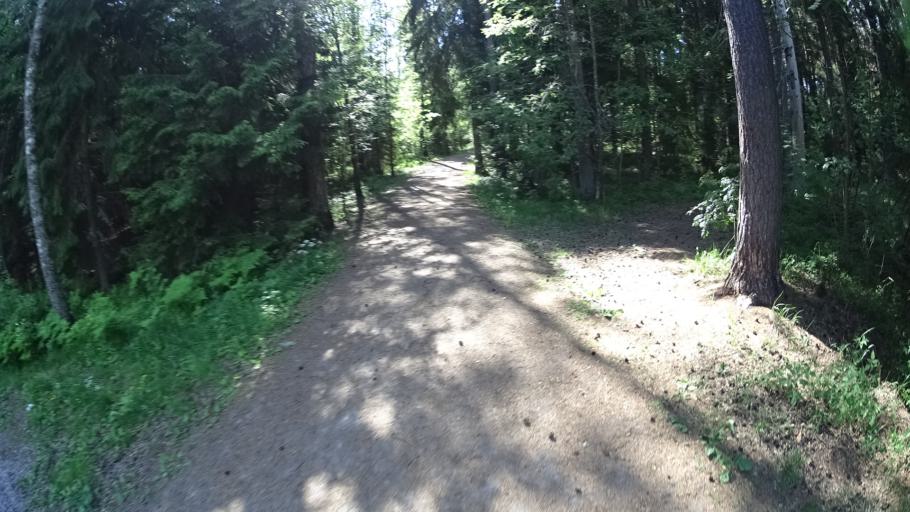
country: FI
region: Uusimaa
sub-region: Helsinki
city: Vantaa
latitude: 60.2350
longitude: 25.1828
